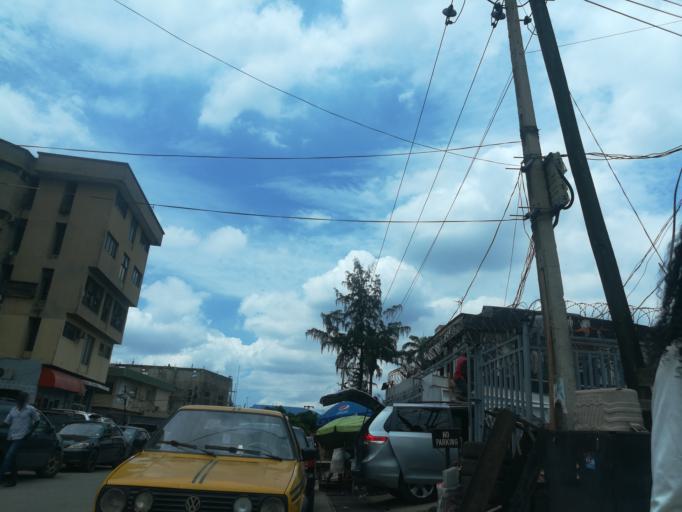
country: NG
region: Lagos
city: Ikeja
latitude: 6.5984
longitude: 3.3535
